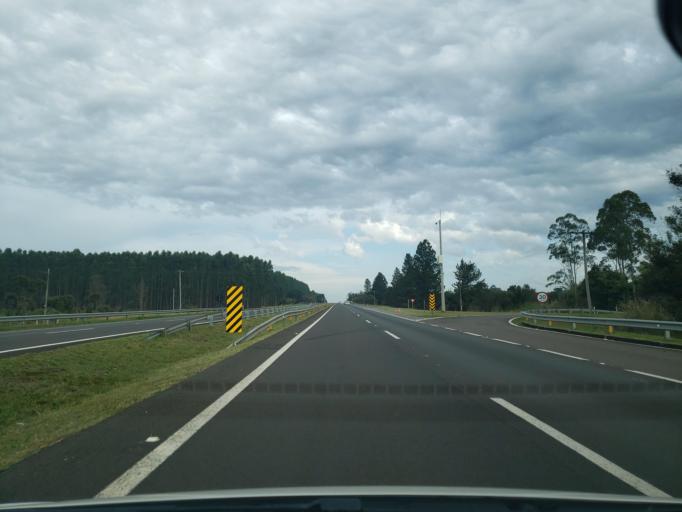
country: BR
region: Sao Paulo
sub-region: Itirapina
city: Itirapina
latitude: -22.2582
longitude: -47.8658
